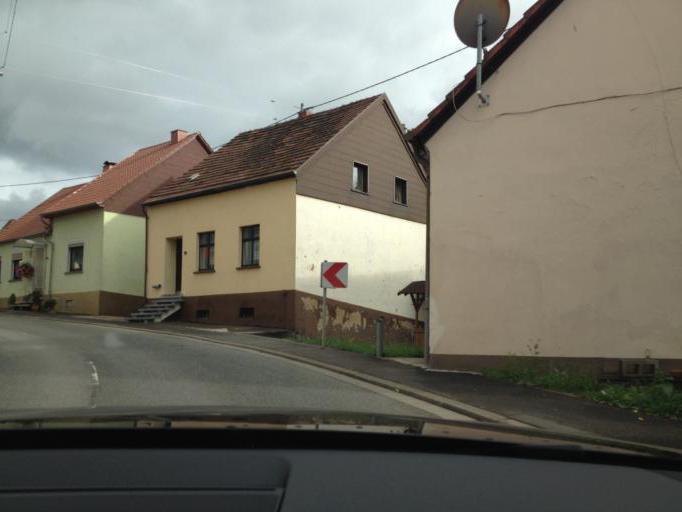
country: DE
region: Saarland
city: Oberthal
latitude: 49.5200
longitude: 7.1052
